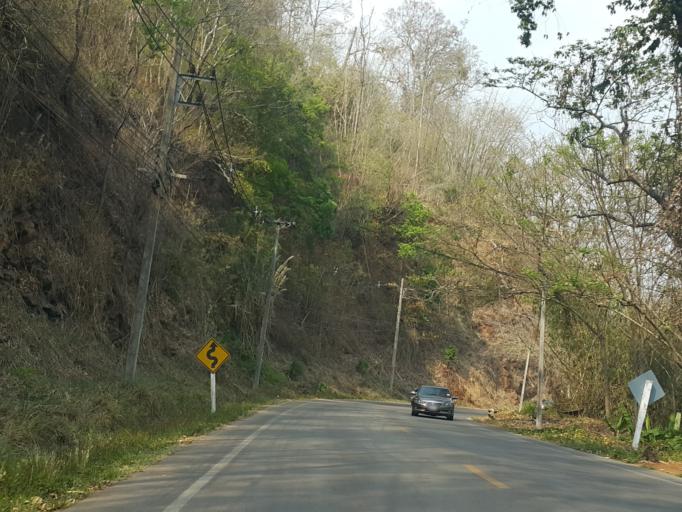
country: TH
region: Chiang Mai
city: Samoeng
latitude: 18.8956
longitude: 98.8417
